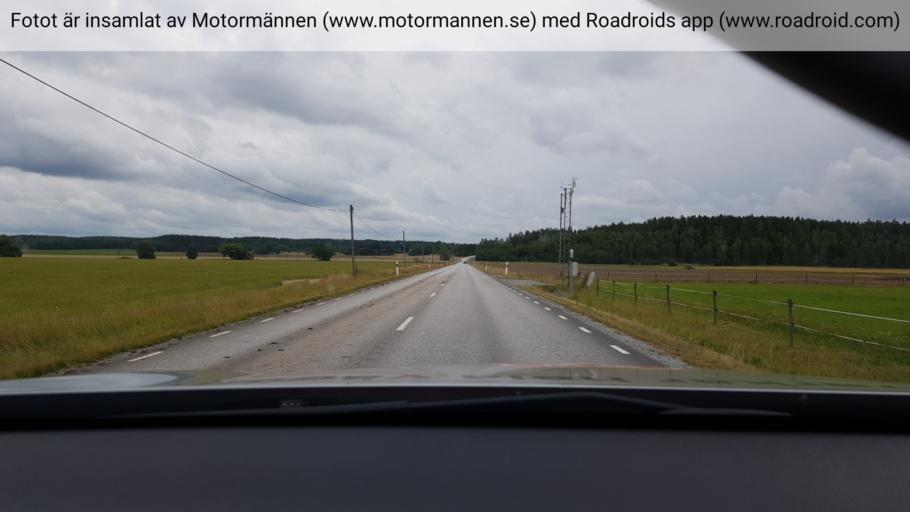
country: SE
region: Stockholm
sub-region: Vallentuna Kommun
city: Vallentuna
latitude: 59.7482
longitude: 18.0465
